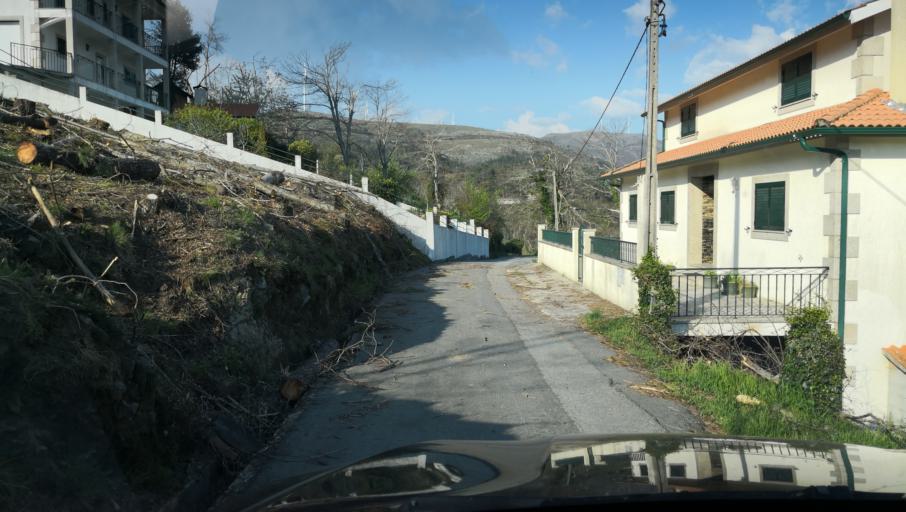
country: PT
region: Vila Real
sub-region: Mondim de Basto
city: Mondim de Basto
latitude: 41.3147
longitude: -7.8782
